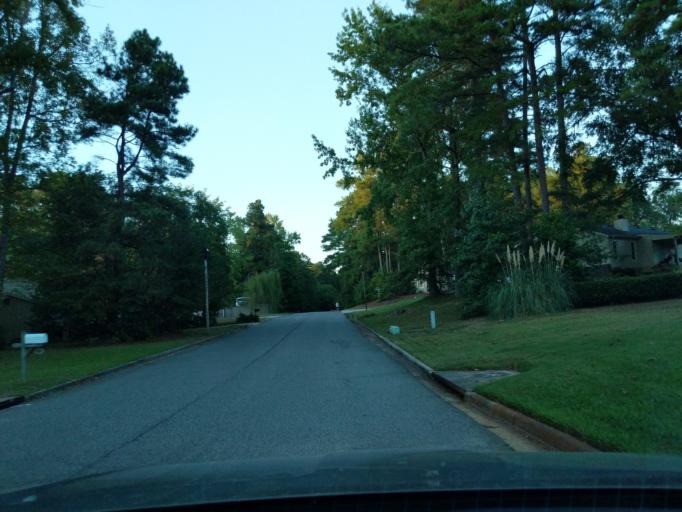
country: US
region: Georgia
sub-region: Columbia County
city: Martinez
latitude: 33.5270
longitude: -82.0894
